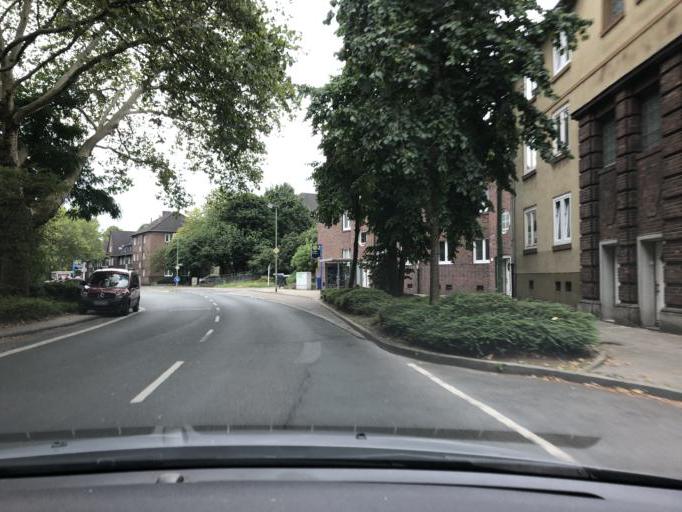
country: DE
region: North Rhine-Westphalia
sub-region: Regierungsbezirk Munster
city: Bottrop
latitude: 51.4730
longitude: 6.9417
